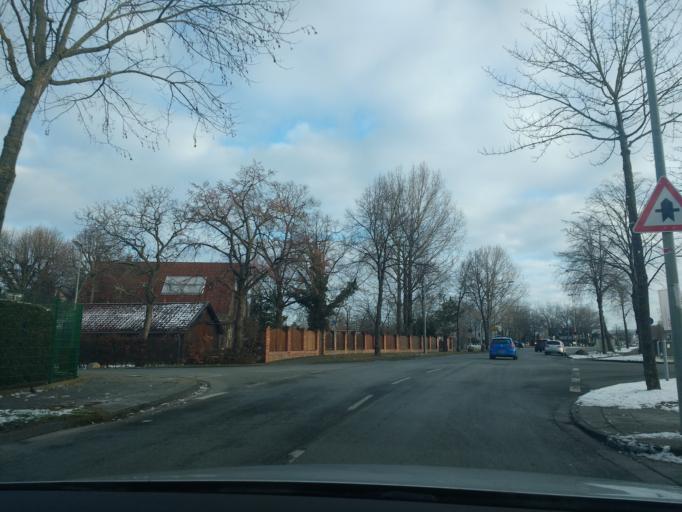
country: DE
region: North Rhine-Westphalia
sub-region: Regierungsbezirk Detmold
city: Paderborn
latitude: 51.7374
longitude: 8.7851
